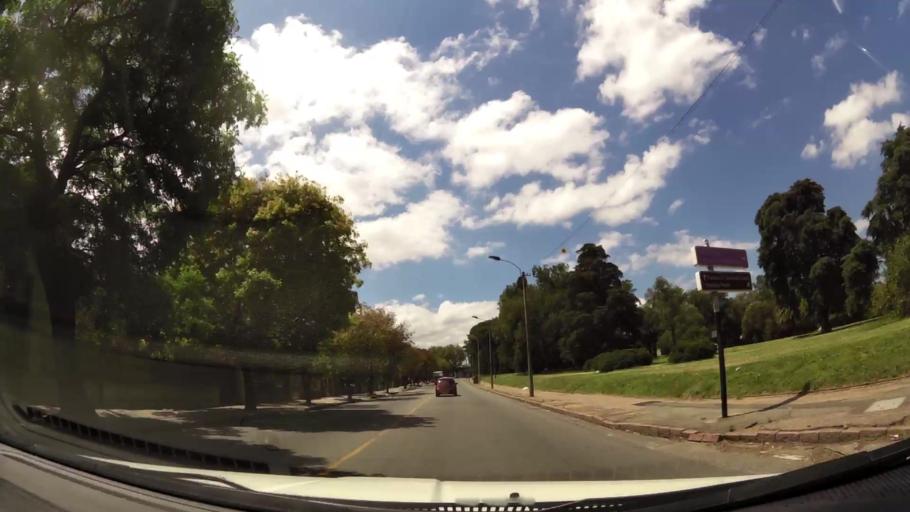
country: UY
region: Montevideo
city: Montevideo
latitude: -34.8575
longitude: -56.2125
